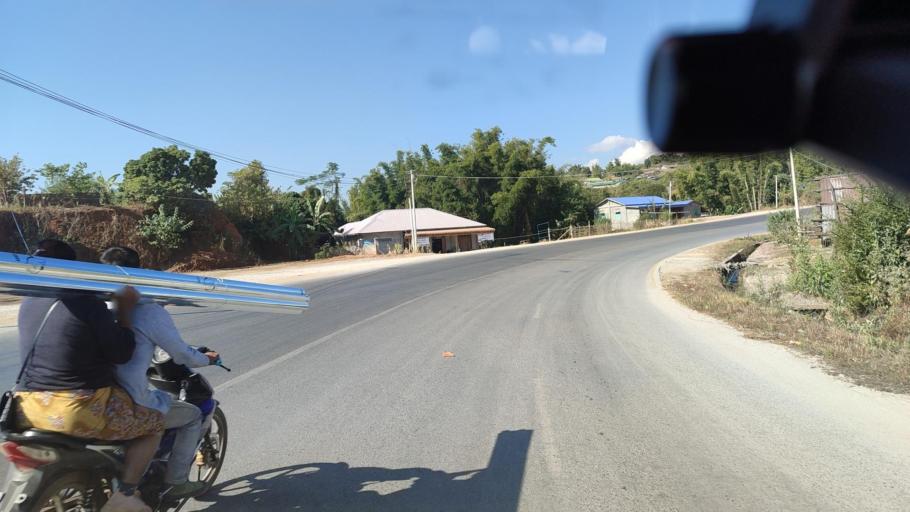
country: MM
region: Shan
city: Lashio
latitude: 23.3242
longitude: 97.9681
